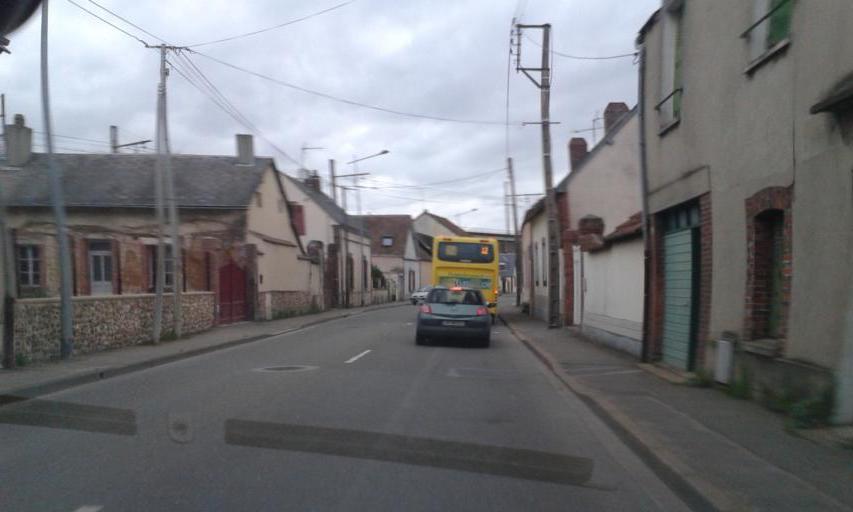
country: FR
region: Centre
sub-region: Departement d'Eure-et-Loir
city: Leves
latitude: 48.4609
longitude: 1.4828
